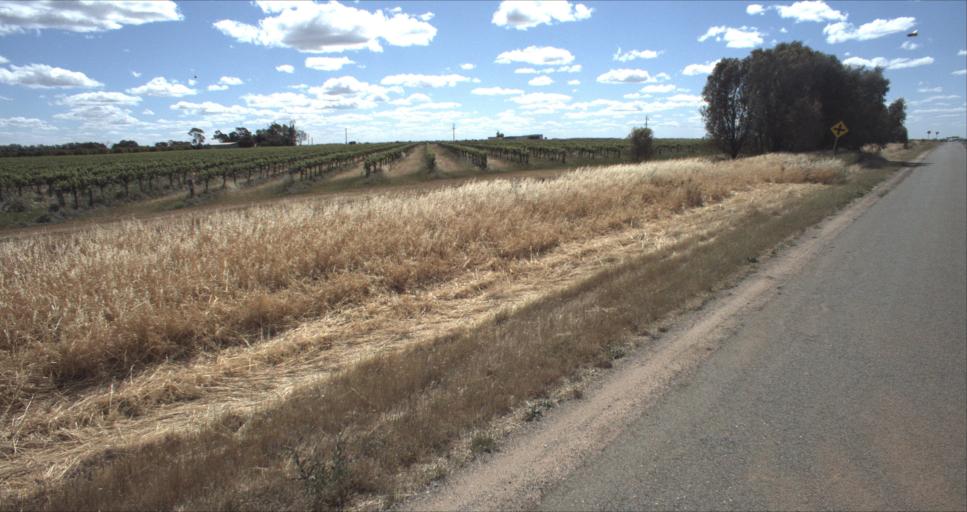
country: AU
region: New South Wales
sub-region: Leeton
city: Leeton
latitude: -34.5069
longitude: 146.2220
